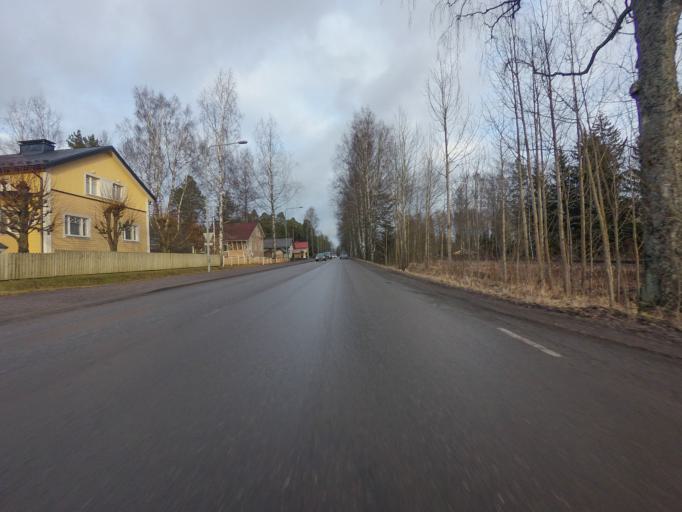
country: FI
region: Uusimaa
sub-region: Helsinki
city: Lohja
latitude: 60.2505
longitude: 24.0934
